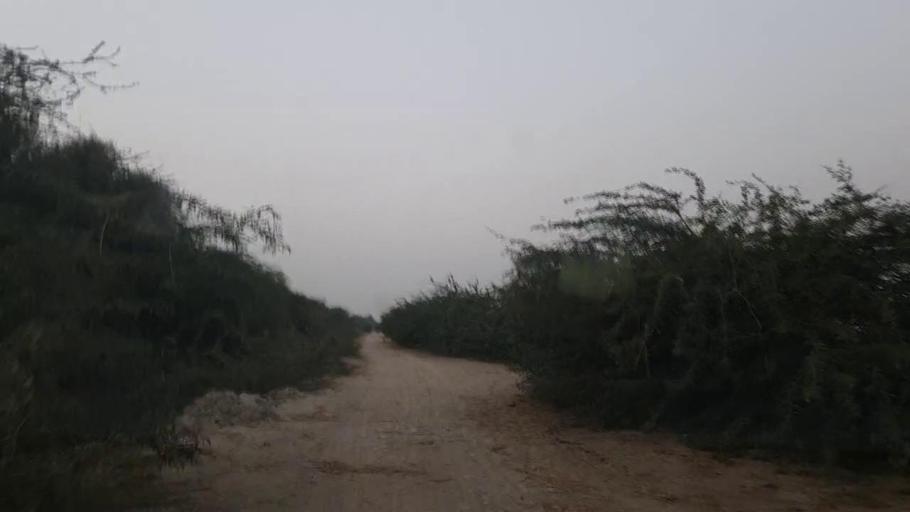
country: PK
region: Sindh
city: Mirpur Sakro
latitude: 24.5767
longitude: 67.7864
